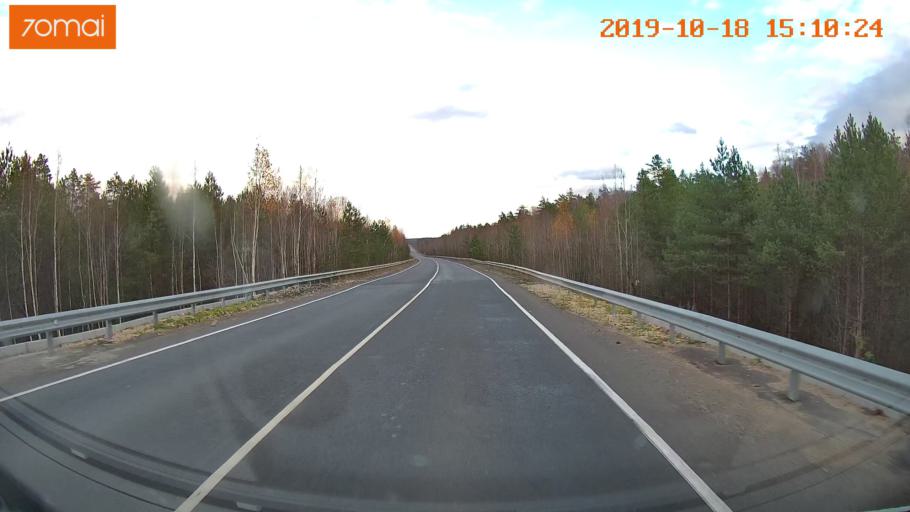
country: RU
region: Vladimir
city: Gus'-Khrustal'nyy
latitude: 55.5677
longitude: 40.6436
